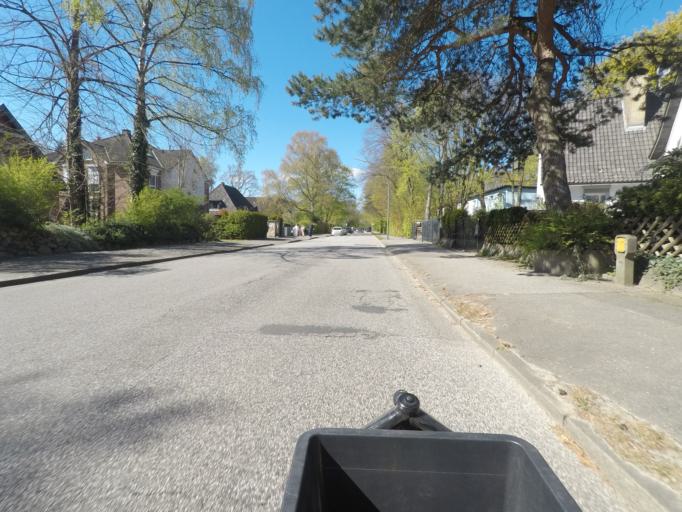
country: DE
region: Hamburg
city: Farmsen-Berne
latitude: 53.6040
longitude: 10.1088
